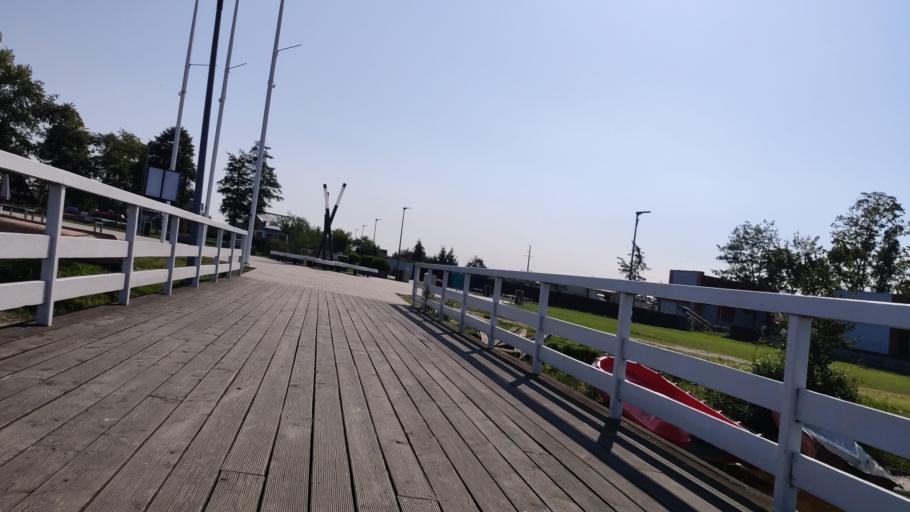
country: PL
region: Kujawsko-Pomorskie
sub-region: Powiat zninski
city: Znin
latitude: 52.8429
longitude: 17.7239
